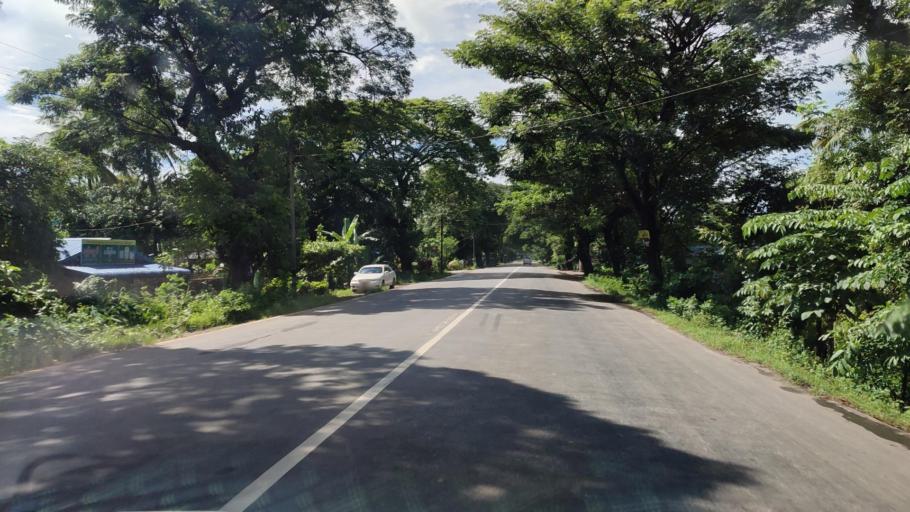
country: MM
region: Bago
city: Pyu
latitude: 18.2489
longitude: 96.5346
